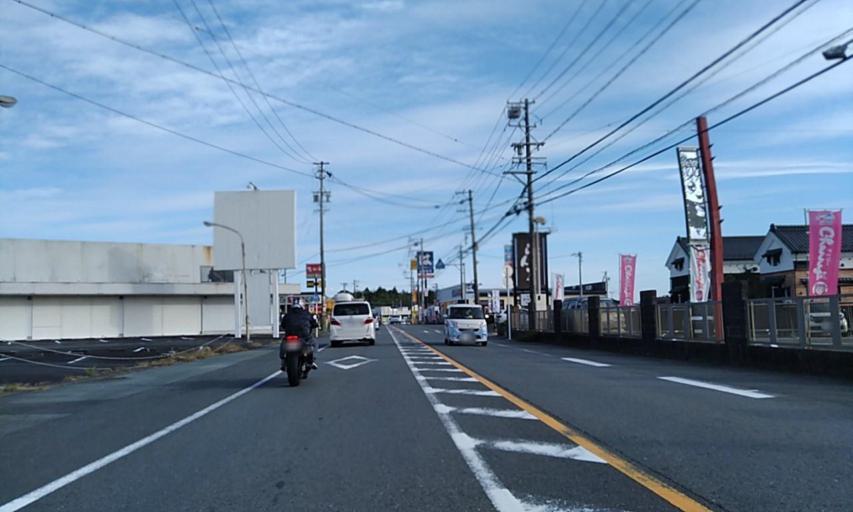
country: JP
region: Mie
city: Toba
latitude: 34.3455
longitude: 136.8137
